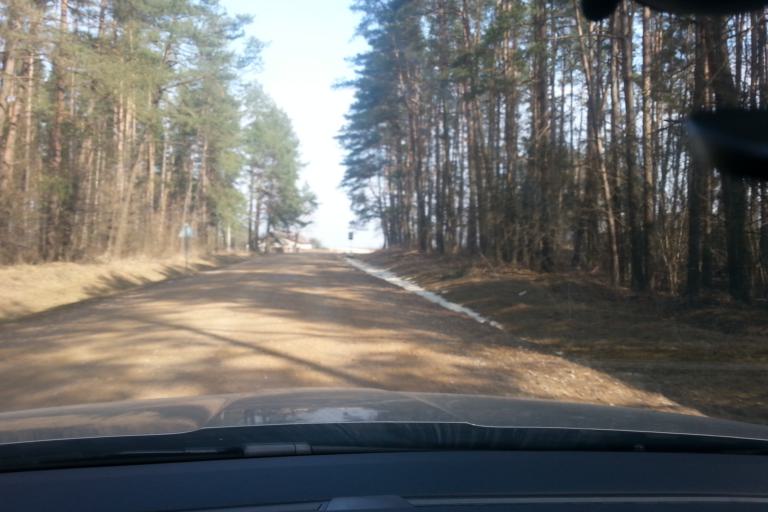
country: LT
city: Trakai
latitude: 54.5818
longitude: 24.9743
